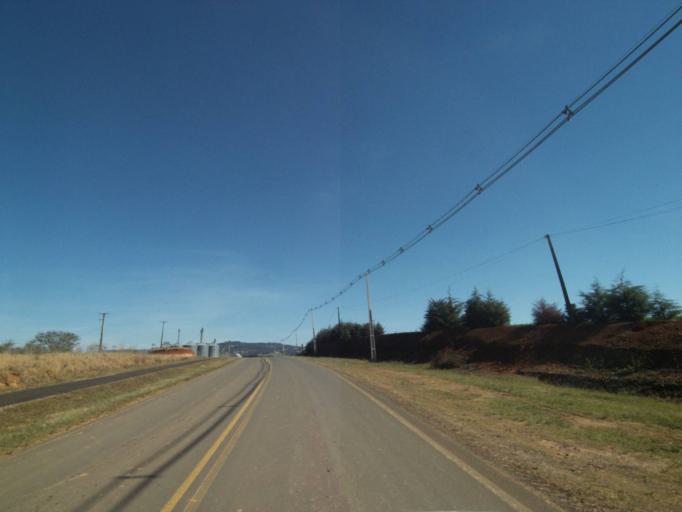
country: BR
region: Parana
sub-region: Tibagi
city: Tibagi
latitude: -24.5238
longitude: -50.4335
